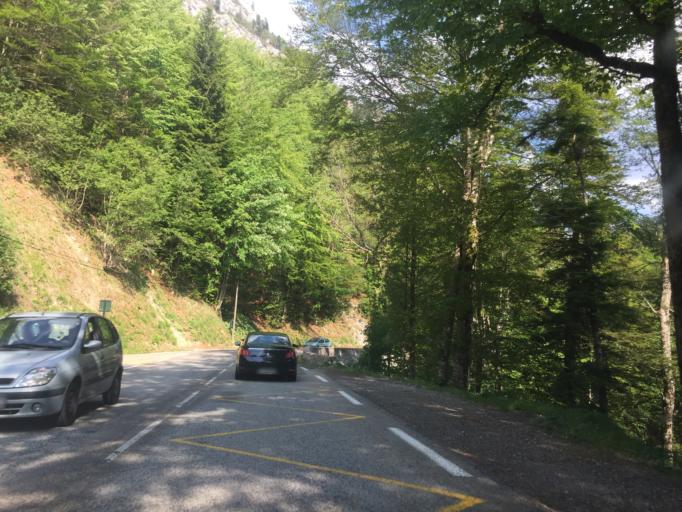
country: FR
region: Rhone-Alpes
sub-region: Departement de l'Isere
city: Saint-Laurent-du-Pont
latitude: 45.3467
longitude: 5.7940
